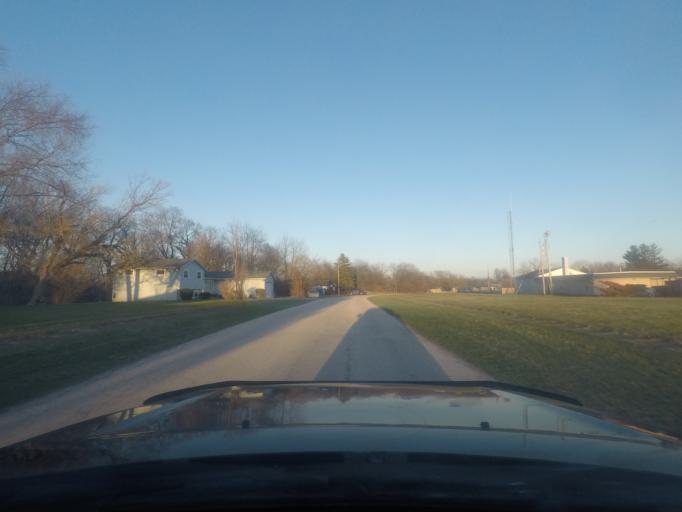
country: US
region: Indiana
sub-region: LaPorte County
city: Kingsford Heights
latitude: 41.4834
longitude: -86.6922
